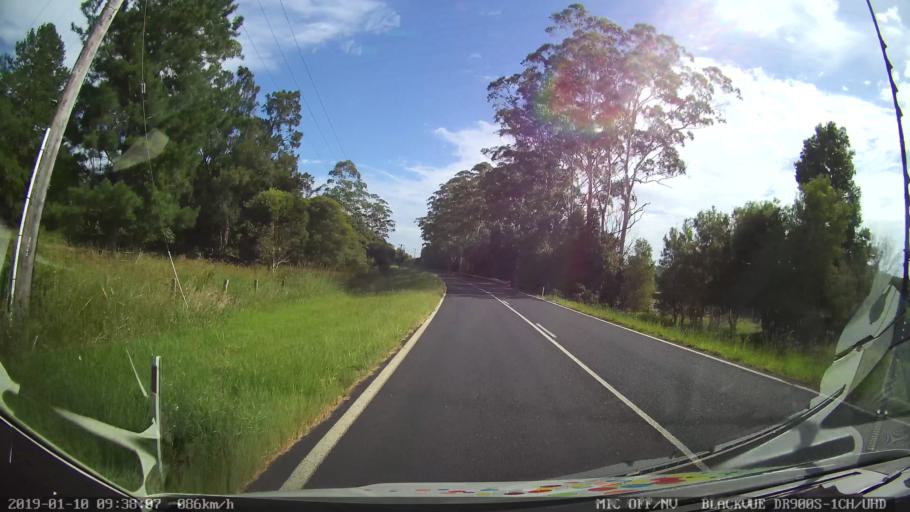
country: AU
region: New South Wales
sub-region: Coffs Harbour
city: Nana Glen
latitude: -30.1798
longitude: 153.0074
